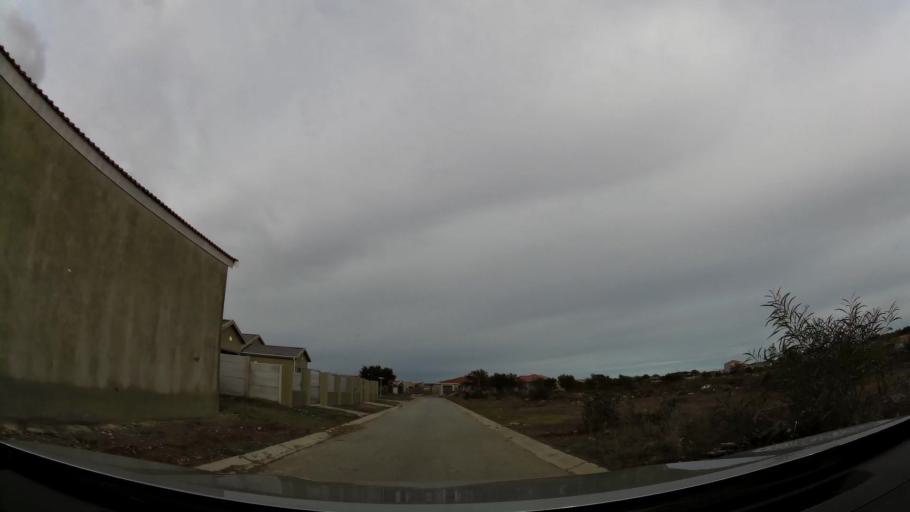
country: ZA
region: Eastern Cape
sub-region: Nelson Mandela Bay Metropolitan Municipality
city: Port Elizabeth
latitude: -33.9299
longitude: 25.5020
